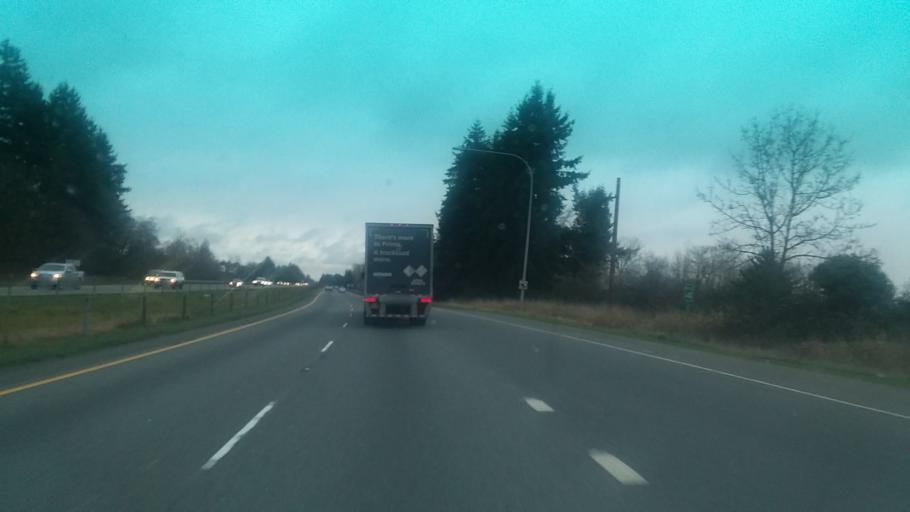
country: US
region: Washington
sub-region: Pierce County
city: Midland
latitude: 47.1581
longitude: -122.3969
